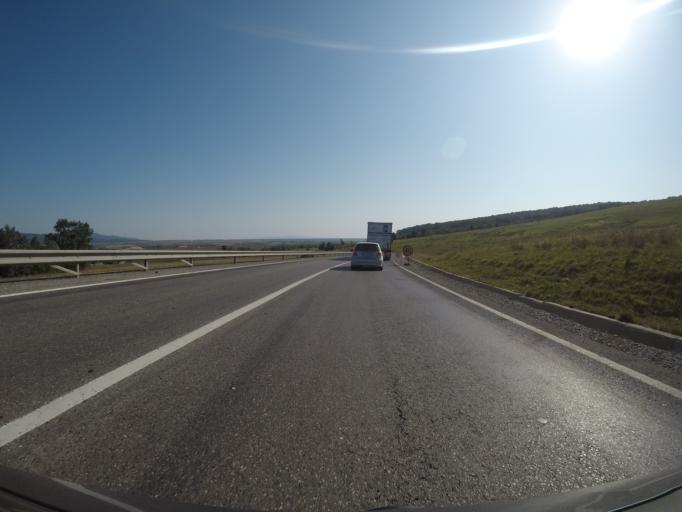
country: RO
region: Brasov
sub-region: Comuna Dumbravita
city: Dumbravita
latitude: 45.7553
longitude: 25.3984
